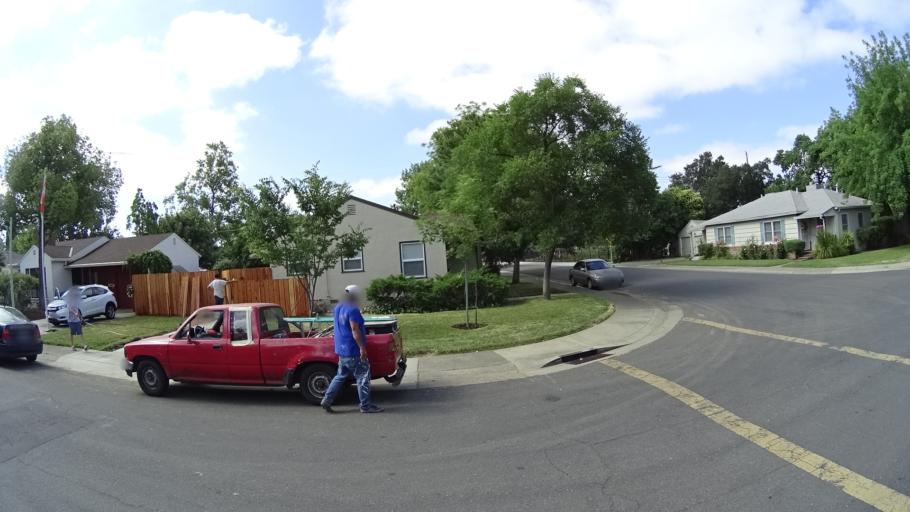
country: US
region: California
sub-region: Sacramento County
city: Parkway
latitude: 38.5316
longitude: -121.4863
